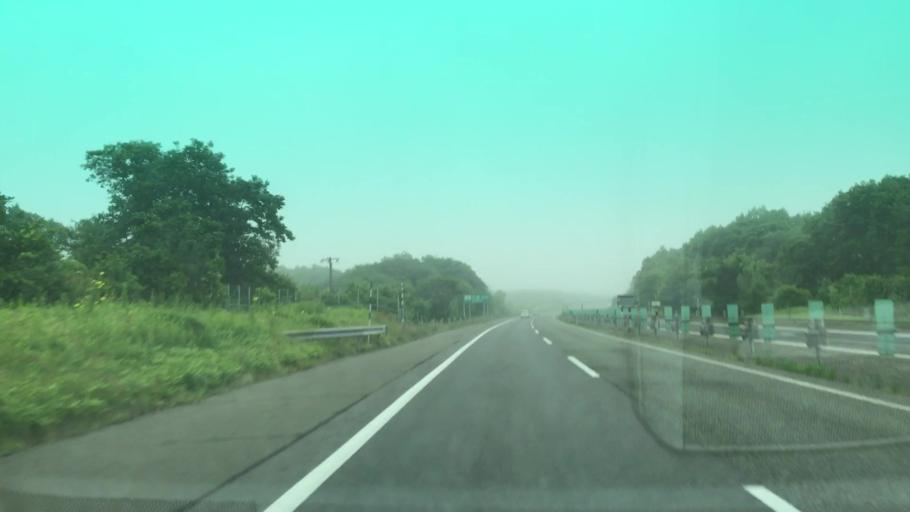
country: JP
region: Hokkaido
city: Chitose
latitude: 42.8311
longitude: 141.6117
